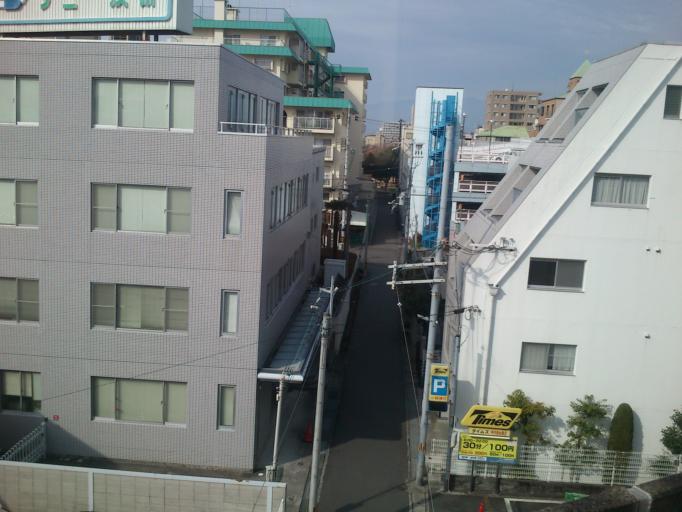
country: JP
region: Hyogo
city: Itami
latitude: 34.7789
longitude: 135.4151
